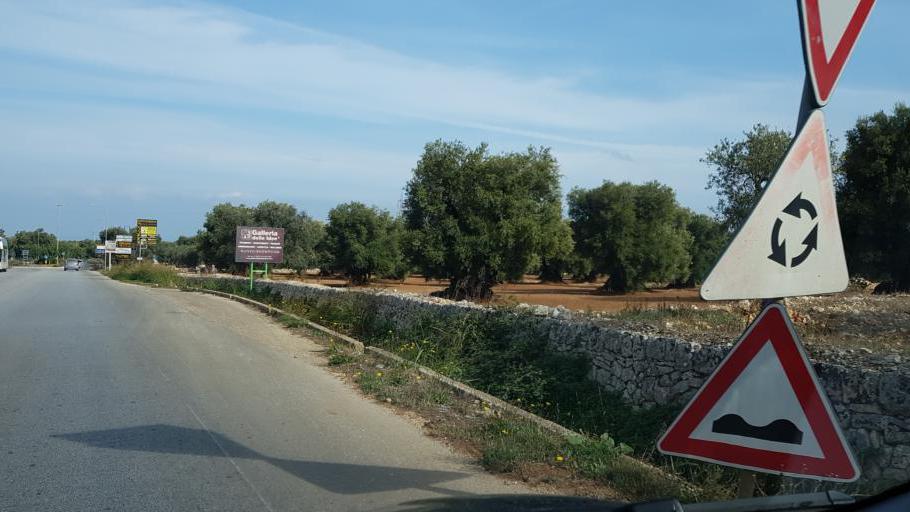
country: IT
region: Apulia
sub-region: Provincia di Brindisi
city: Ostuni
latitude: 40.7428
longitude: 17.5790
